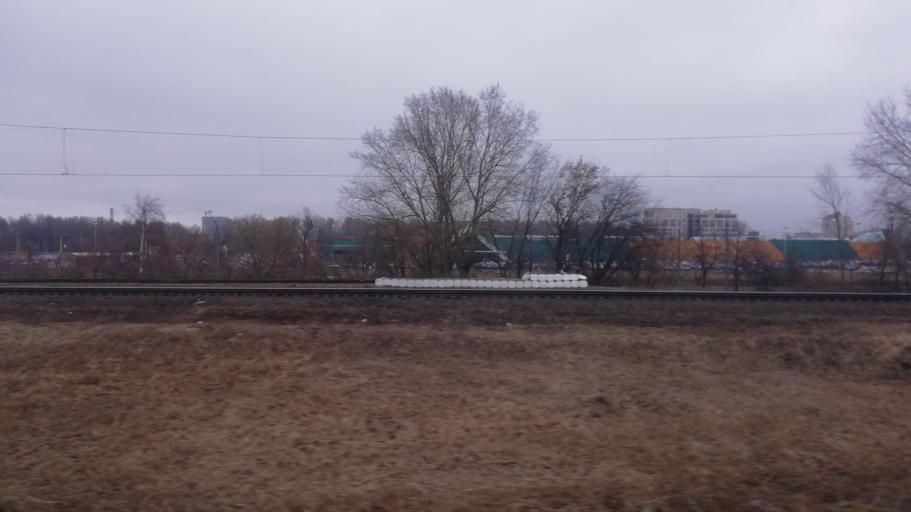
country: RU
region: St.-Petersburg
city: Kupchino
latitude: 59.8770
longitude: 30.3519
